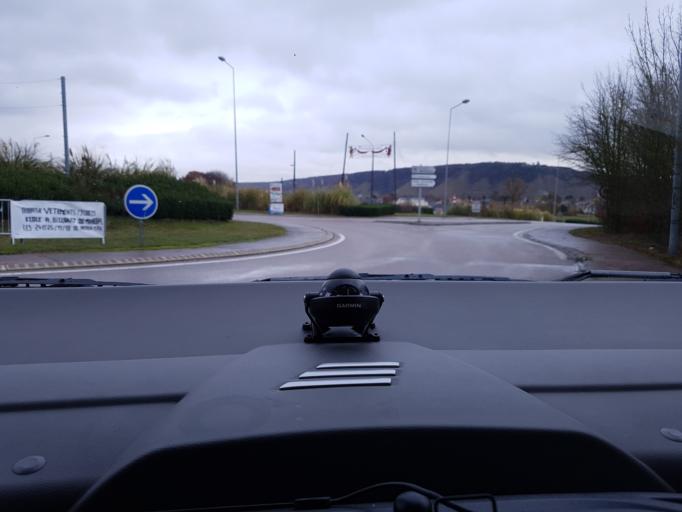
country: FR
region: Haute-Normandie
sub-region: Departement de l'Eure
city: Le Manoir
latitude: 49.3264
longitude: 1.2176
